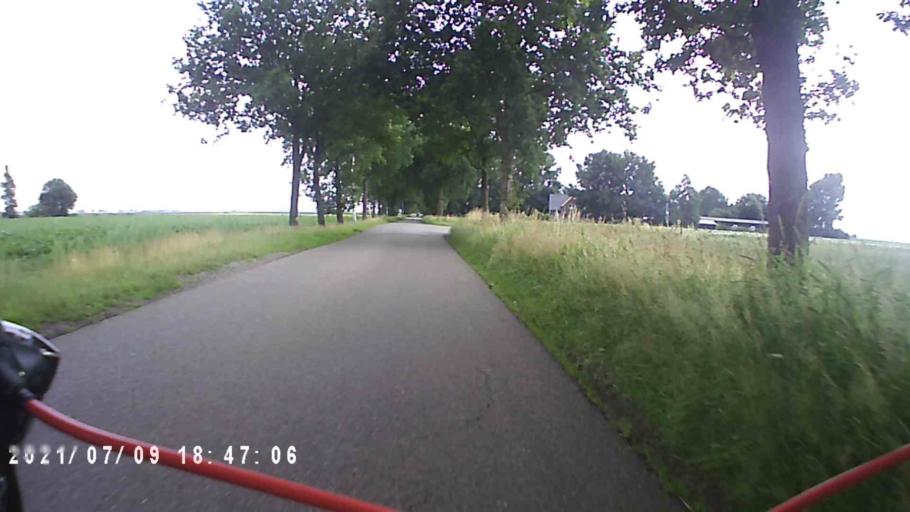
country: NL
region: Groningen
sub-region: Gemeente Veendam
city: Veendam
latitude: 53.0712
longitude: 6.9170
